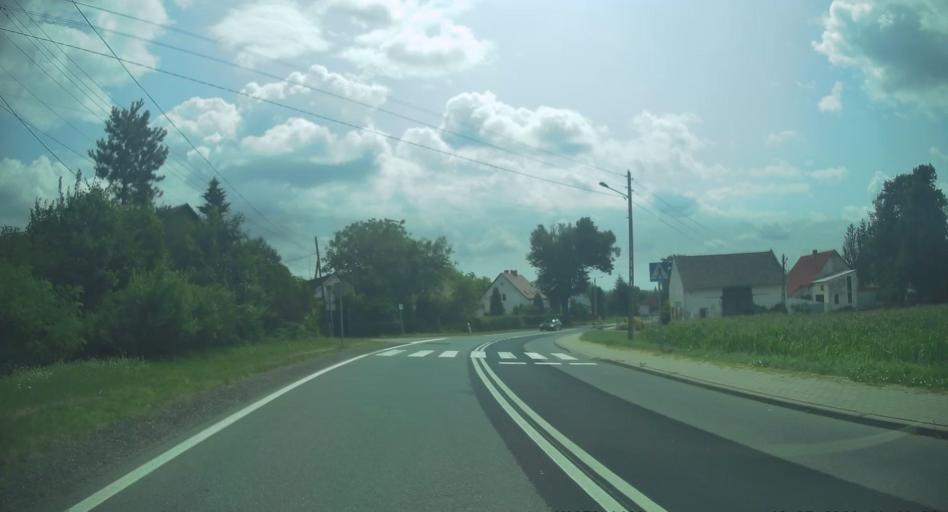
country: PL
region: Opole Voivodeship
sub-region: Powiat prudnicki
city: Prudnik
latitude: 50.3451
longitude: 17.5587
